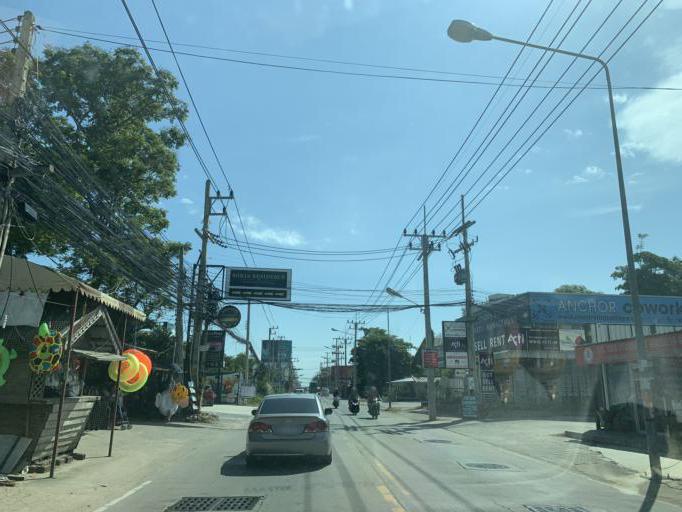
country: TH
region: Chon Buri
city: Phatthaya
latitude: 12.8790
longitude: 100.8909
